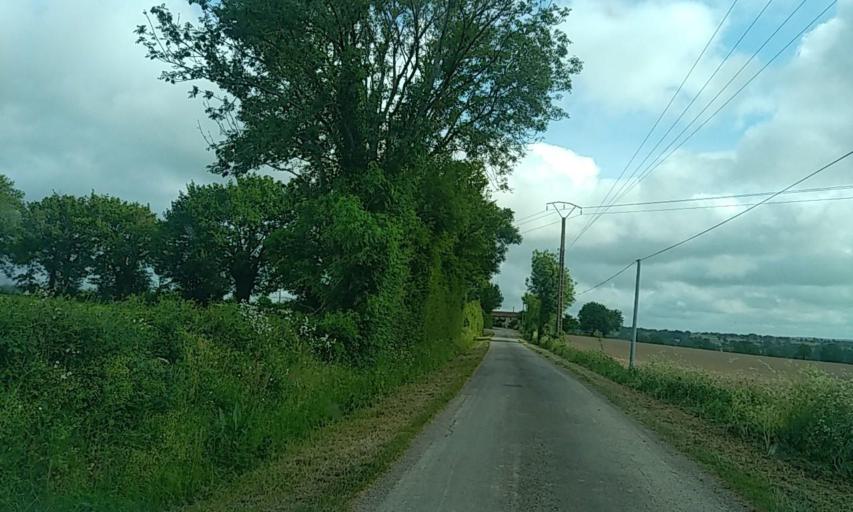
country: FR
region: Poitou-Charentes
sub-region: Departement des Deux-Sevres
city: Boisme
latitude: 46.7628
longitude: -0.4168
